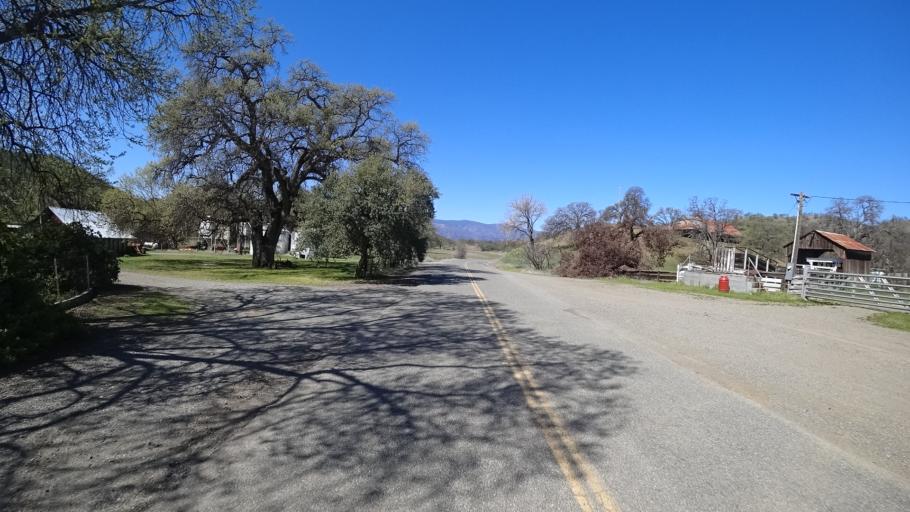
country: US
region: California
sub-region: Tehama County
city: Rancho Tehama Reserve
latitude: 39.7897
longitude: -122.5003
